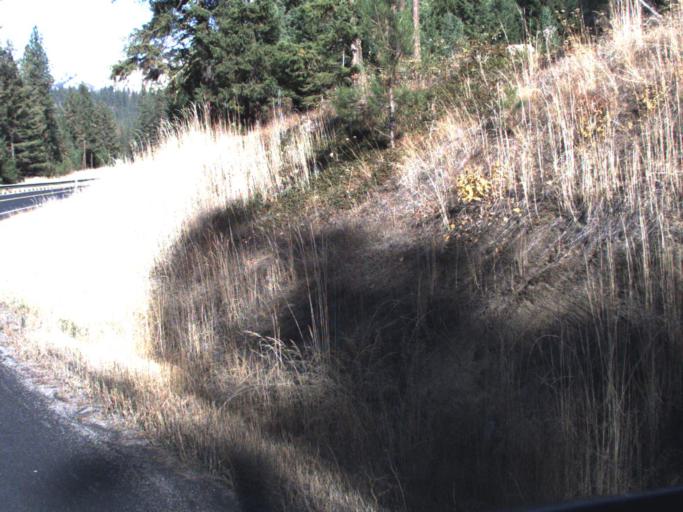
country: US
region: Washington
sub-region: Lincoln County
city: Davenport
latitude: 48.0536
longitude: -118.2229
